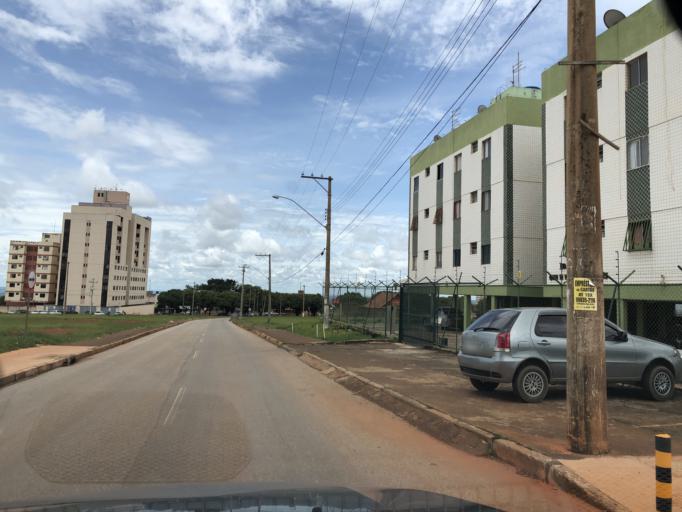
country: BR
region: Federal District
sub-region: Brasilia
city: Brasilia
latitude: -15.8187
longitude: -48.1147
